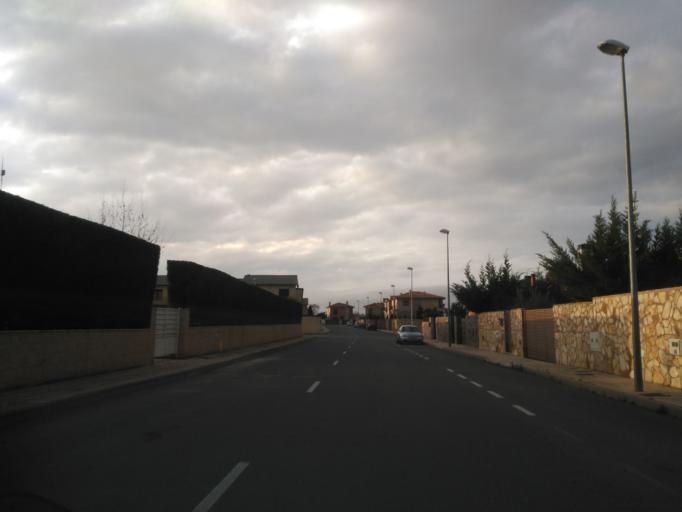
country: ES
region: Castille and Leon
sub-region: Provincia de Salamanca
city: Santa Marta de Tormes
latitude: 40.9316
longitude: -5.6259
